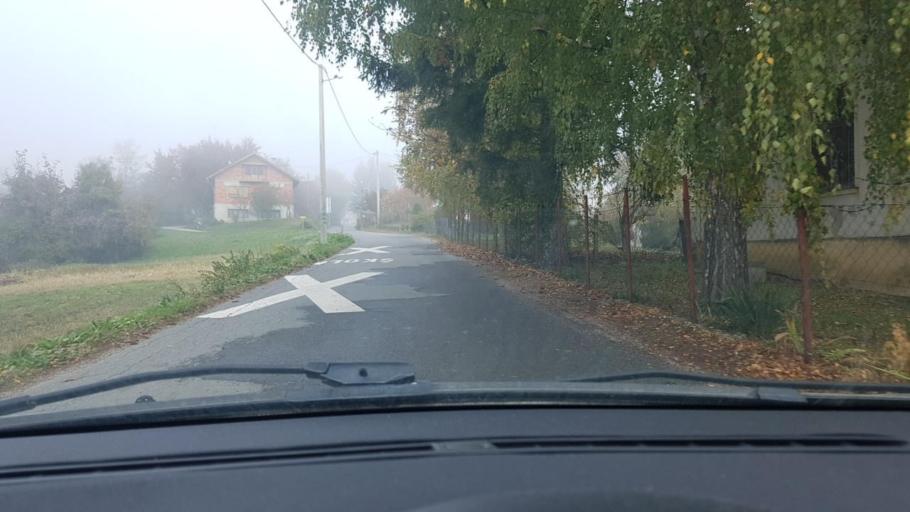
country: HR
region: Krapinsko-Zagorska
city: Mihovljan
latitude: 46.1545
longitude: 15.9901
